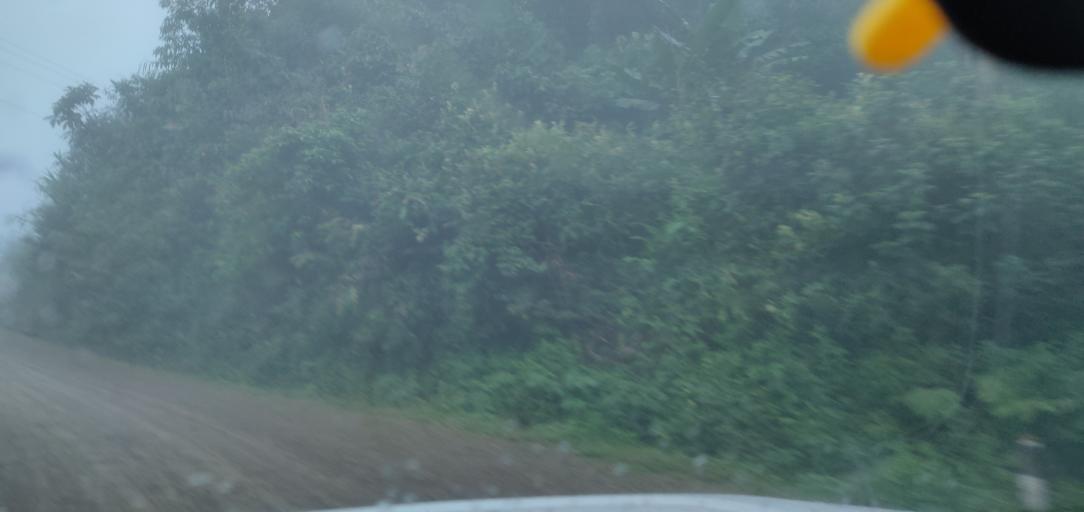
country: LA
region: Phongsali
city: Phongsali
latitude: 21.3934
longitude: 102.1921
